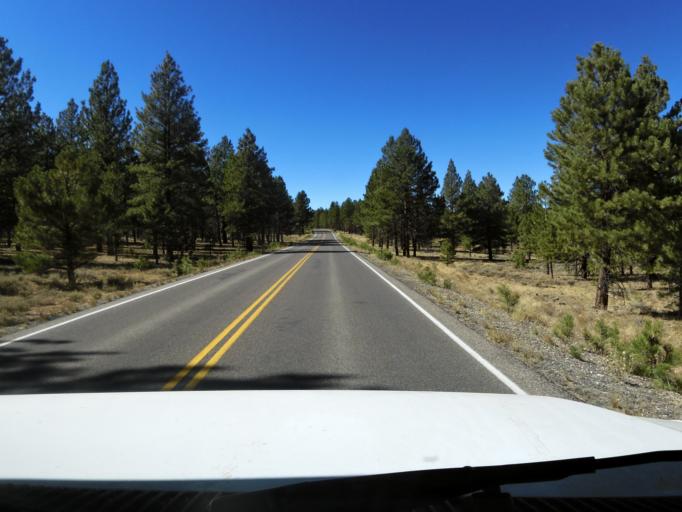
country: US
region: Utah
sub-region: Garfield County
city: Panguitch
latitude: 37.6070
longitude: -112.1933
